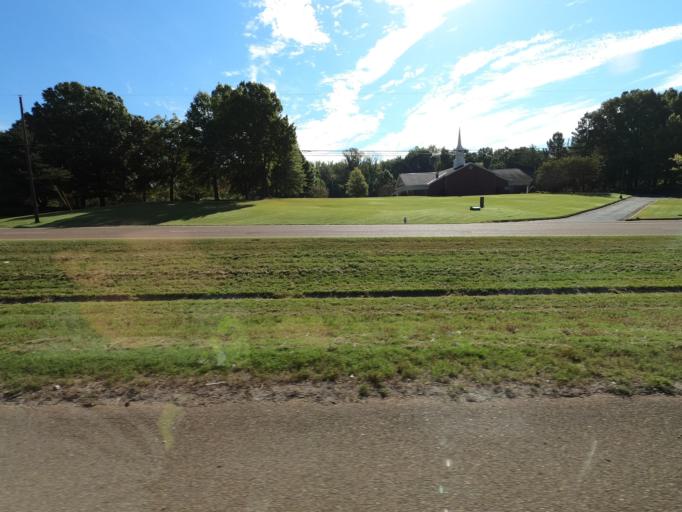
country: US
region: Tennessee
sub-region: Shelby County
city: Millington
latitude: 35.3887
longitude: -89.8568
